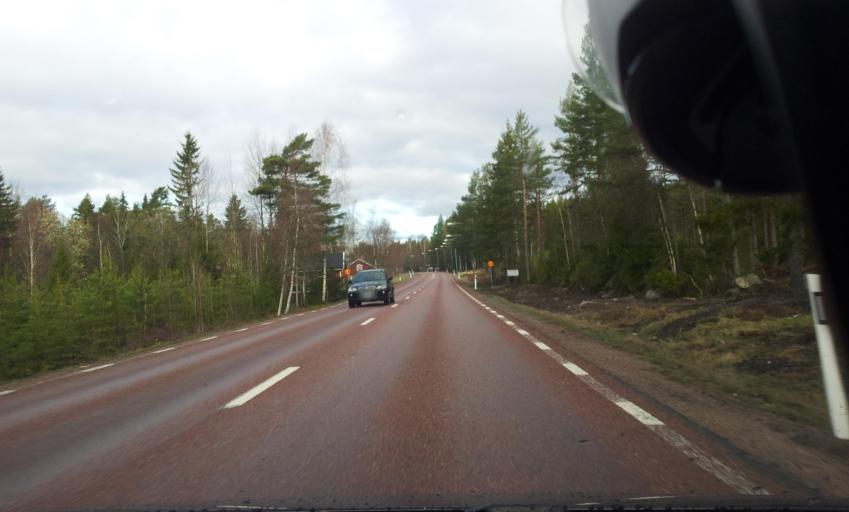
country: SE
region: Gaevleborg
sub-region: Ljusdals Kommun
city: Ljusdal
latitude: 61.8235
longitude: 16.1485
